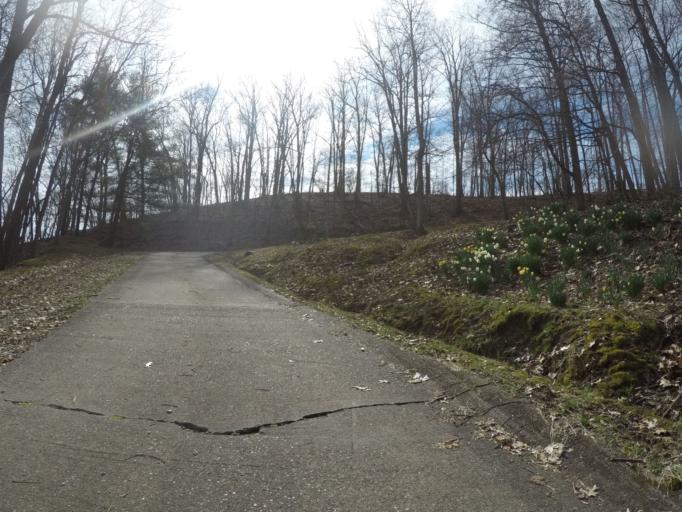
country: US
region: West Virginia
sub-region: Cabell County
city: Barboursville
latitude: 38.3987
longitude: -82.2951
